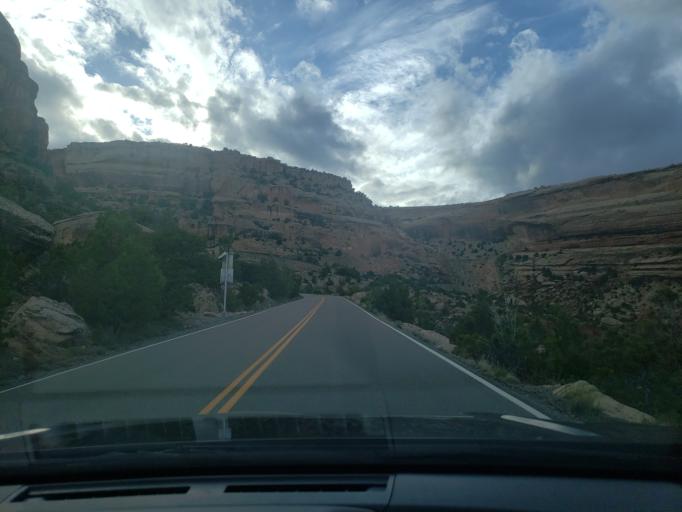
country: US
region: Colorado
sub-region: Mesa County
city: Redlands
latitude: 39.0286
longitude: -108.6423
